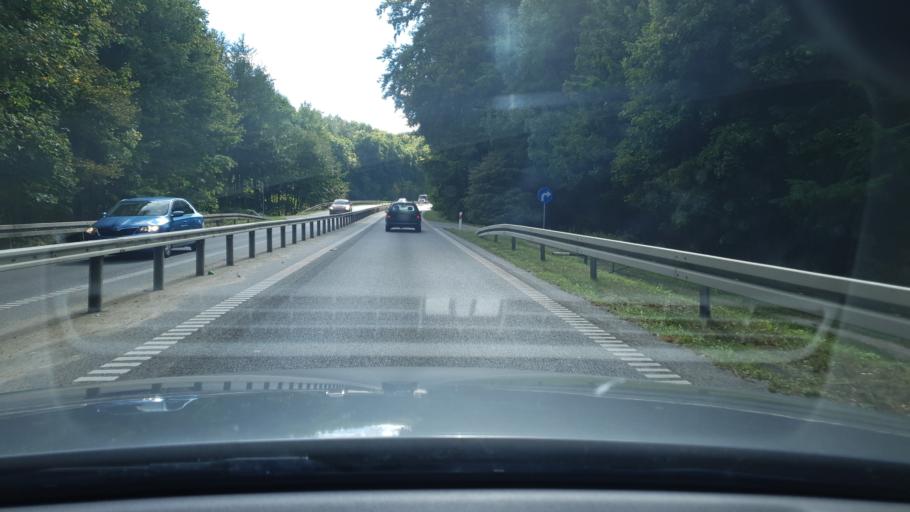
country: PL
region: Pomeranian Voivodeship
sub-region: Powiat wejherowski
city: Reda
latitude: 54.6256
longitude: 18.3412
